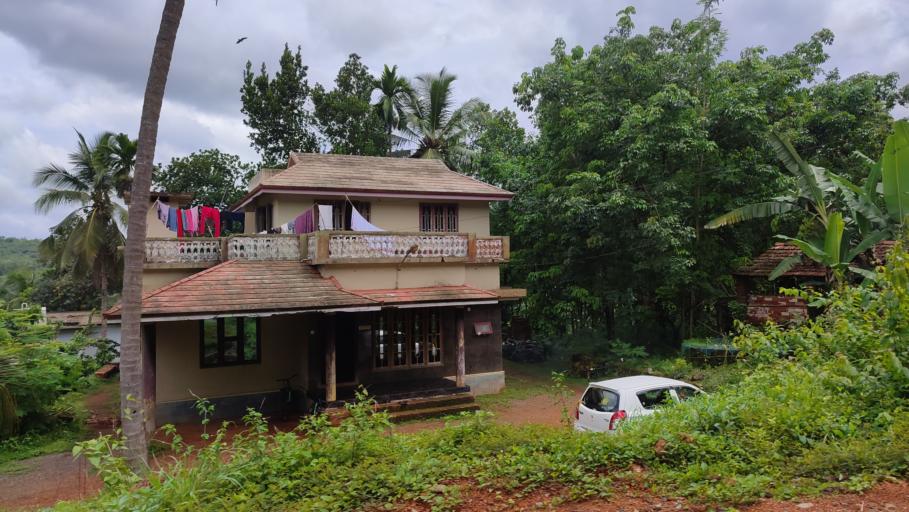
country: IN
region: Kerala
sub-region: Kasaragod District
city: Nileshwar
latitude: 12.2831
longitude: 75.2619
